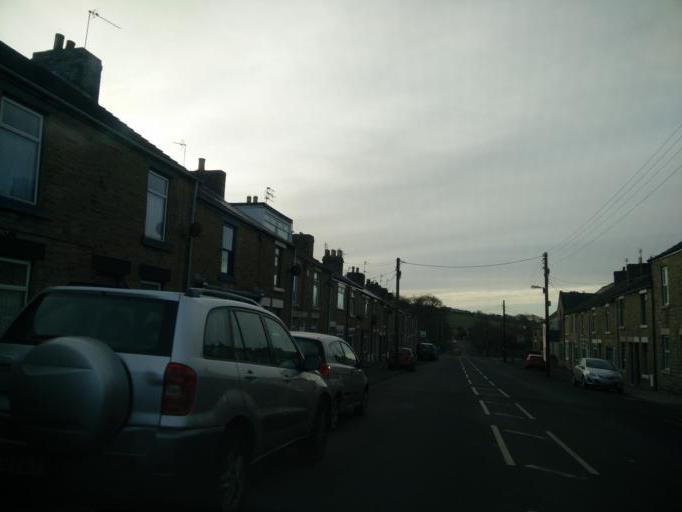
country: GB
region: England
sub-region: County Durham
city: Crook
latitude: 54.6950
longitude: -1.7491
